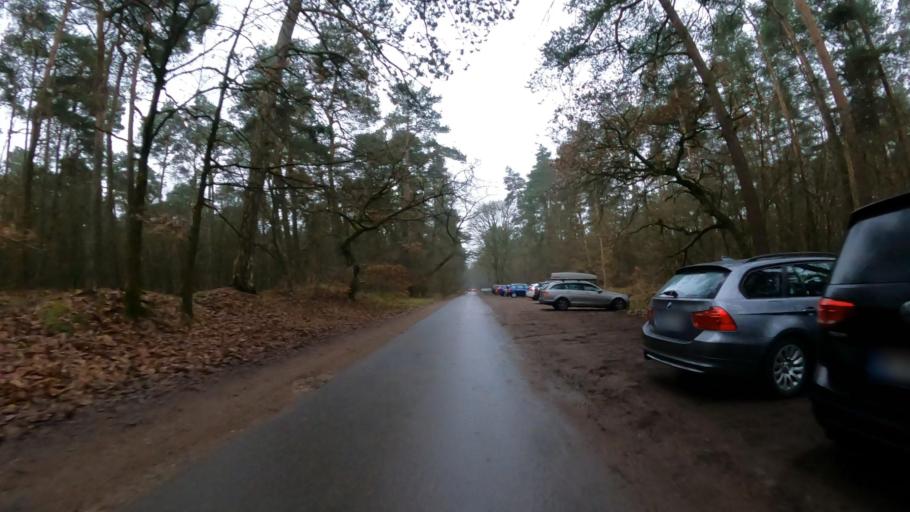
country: DE
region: Schleswig-Holstein
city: Appen
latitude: 53.6003
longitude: 9.7662
